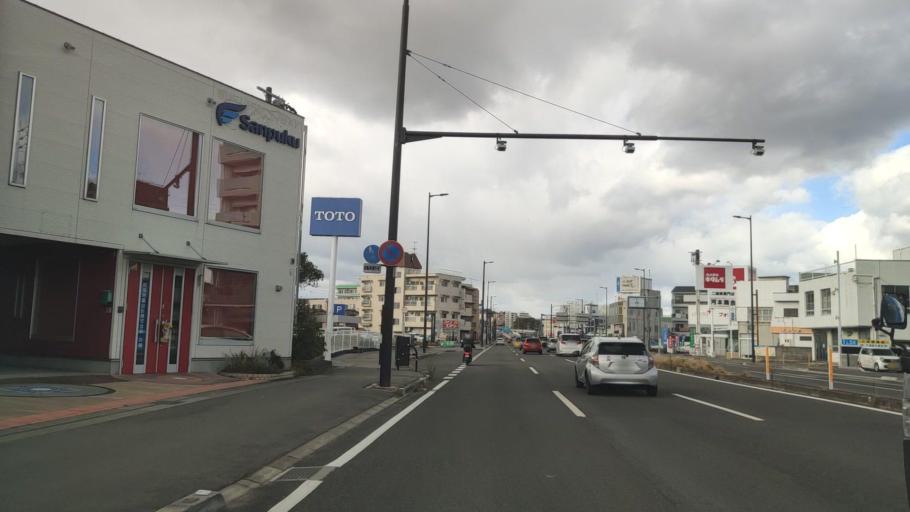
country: JP
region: Ehime
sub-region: Shikoku-chuo Shi
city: Matsuyama
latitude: 33.8299
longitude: 132.7806
